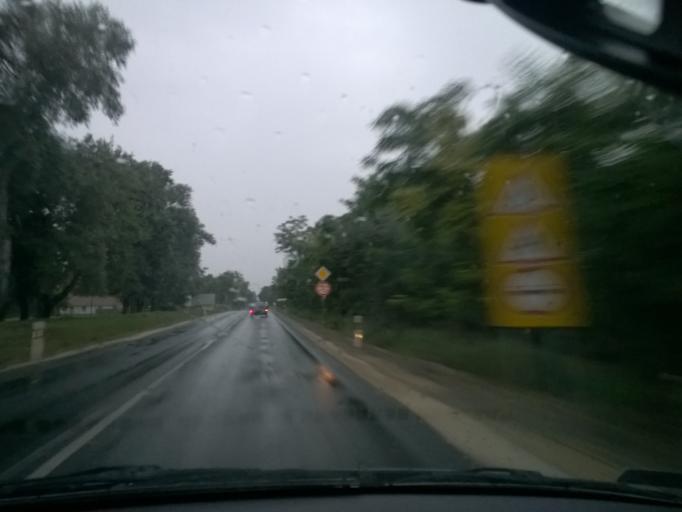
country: HU
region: Pest
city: Kiskunlachaza
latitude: 47.2329
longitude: 19.0210
